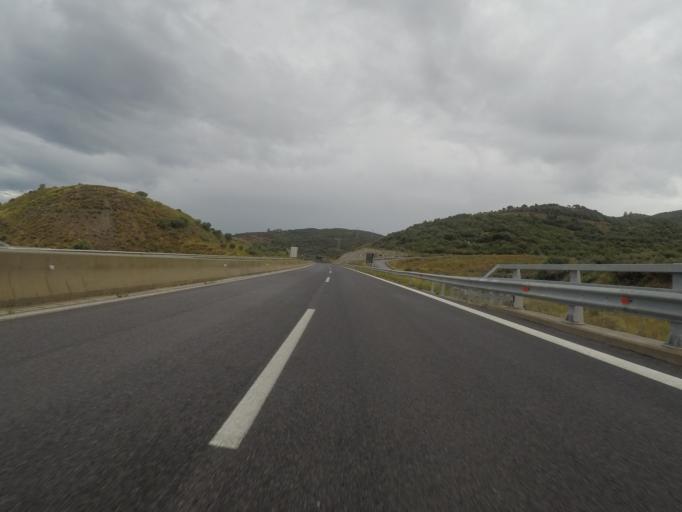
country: GR
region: Peloponnese
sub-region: Nomos Messinias
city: Meligalas
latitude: 37.2599
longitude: 22.0254
